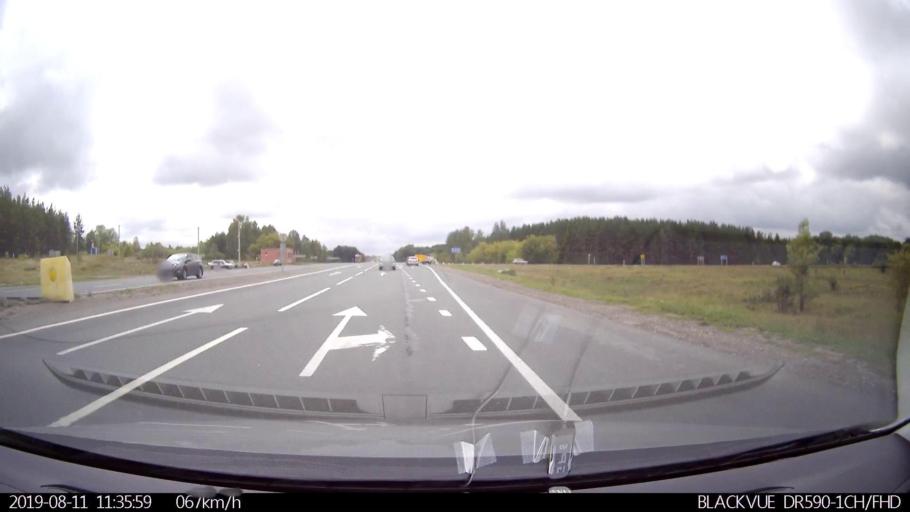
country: RU
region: Ulyanovsk
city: Silikatnyy
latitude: 54.0008
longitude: 48.2210
